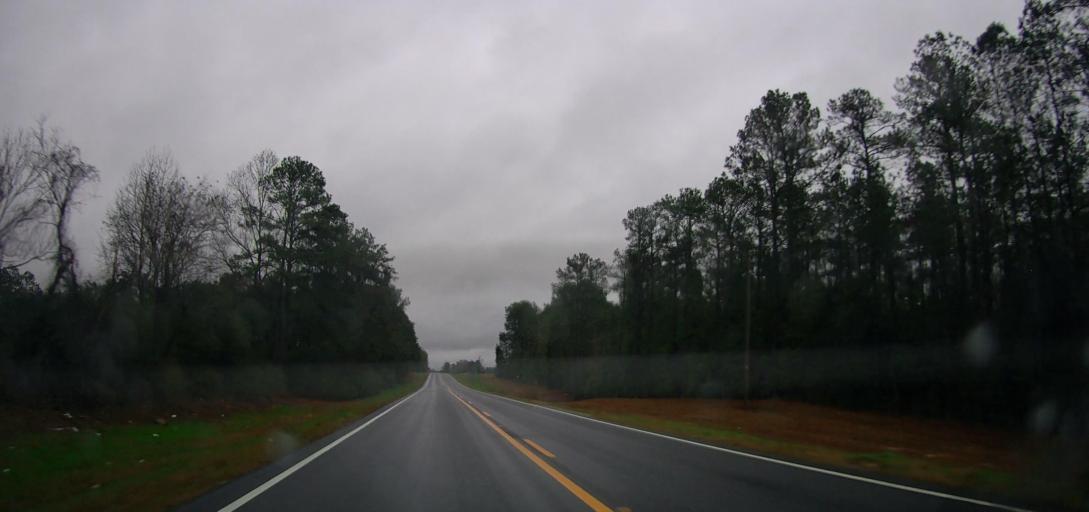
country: US
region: Alabama
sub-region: Bibb County
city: Centreville
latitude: 32.8114
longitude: -86.9289
